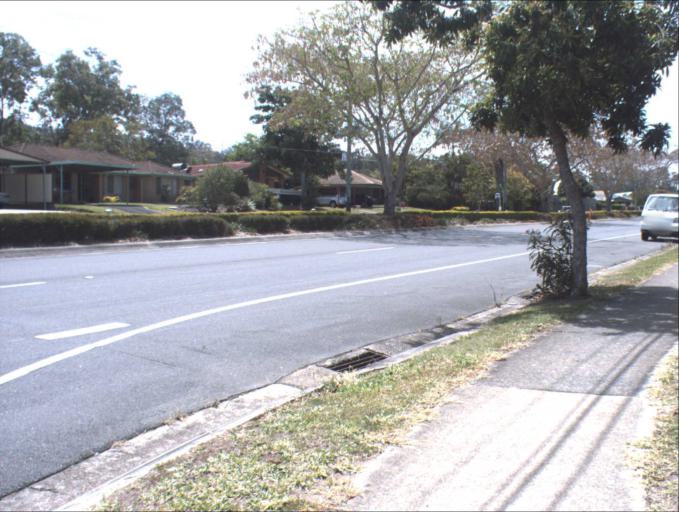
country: AU
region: Queensland
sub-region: Logan
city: Slacks Creek
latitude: -27.6345
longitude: 153.1428
